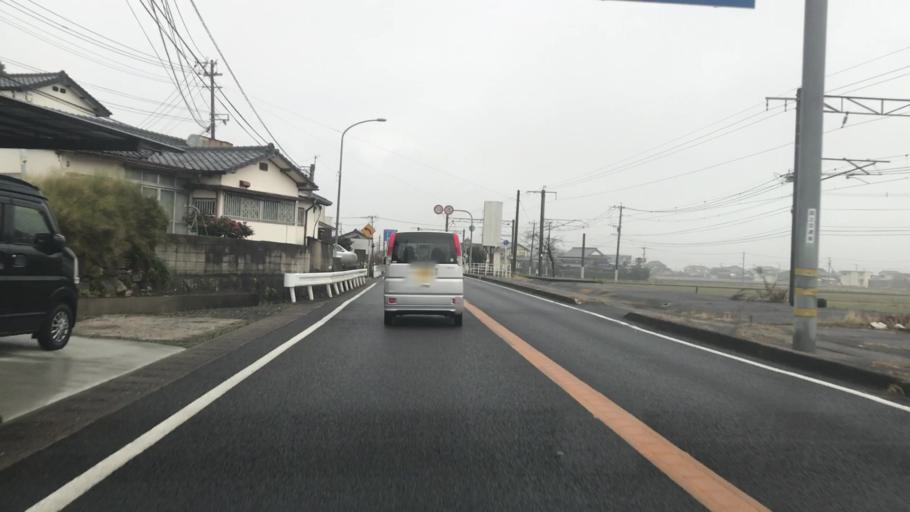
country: JP
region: Saga Prefecture
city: Takeocho-takeo
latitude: 33.2133
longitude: 130.1010
